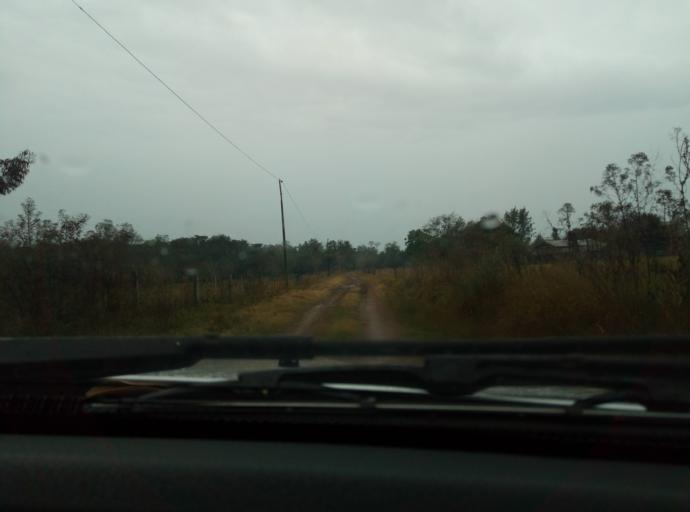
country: PY
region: Caaguazu
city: Carayao
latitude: -25.1045
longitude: -56.4161
